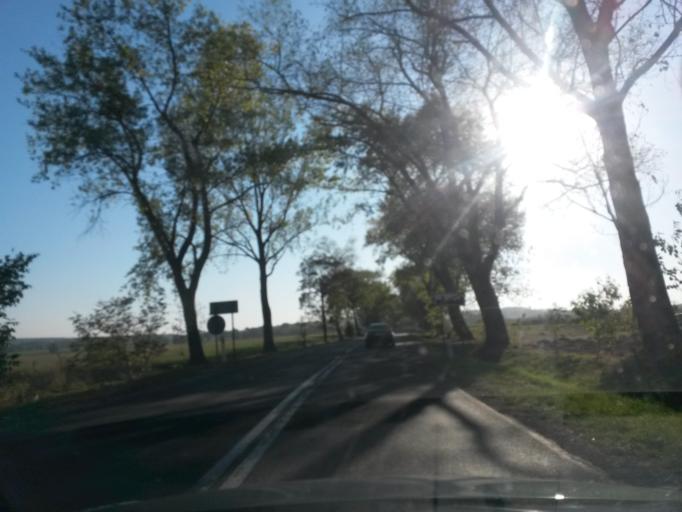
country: PL
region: Lower Silesian Voivodeship
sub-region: Powiat sredzki
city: Udanin
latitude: 51.0160
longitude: 16.4003
